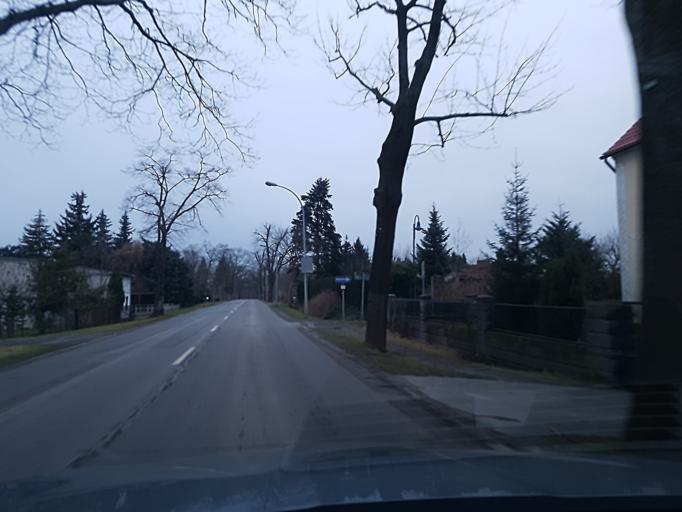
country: DE
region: Brandenburg
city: Finsterwalde
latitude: 51.6438
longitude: 13.6953
